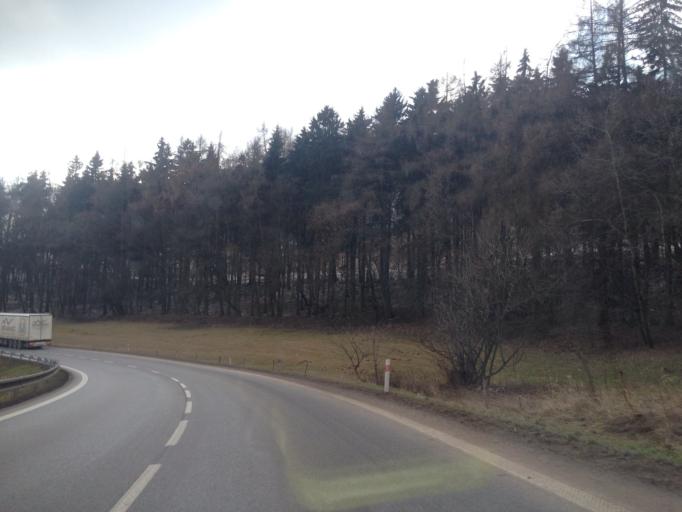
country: CZ
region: Liberecky
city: Studenec
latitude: 50.5204
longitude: 15.5642
